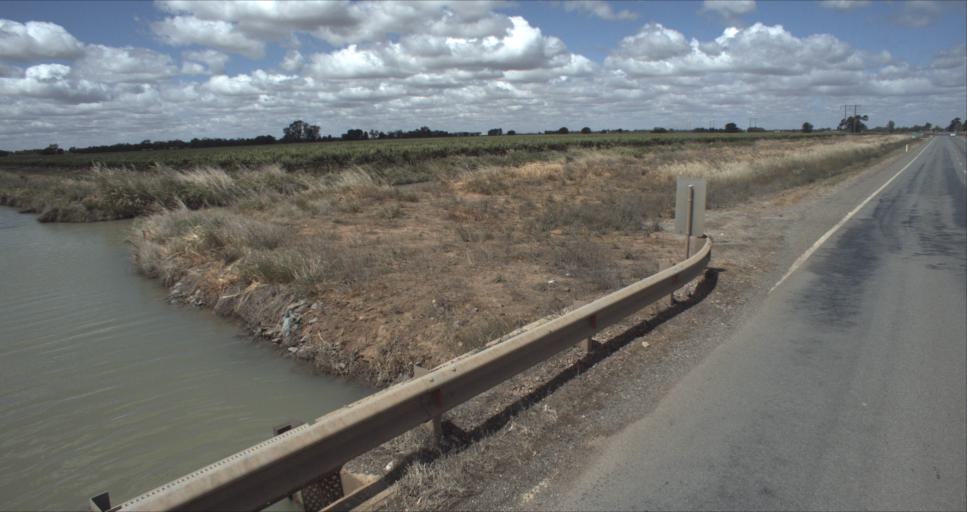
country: AU
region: New South Wales
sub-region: Murrumbidgee Shire
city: Darlington Point
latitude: -34.5041
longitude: 146.1875
